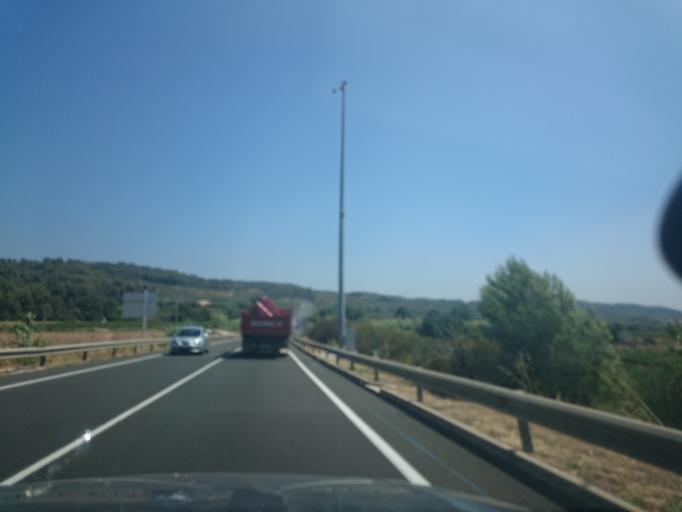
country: ES
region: Catalonia
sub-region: Provincia de Barcelona
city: Sant Pere de Riudebitlles
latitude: 41.4539
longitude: 1.6873
